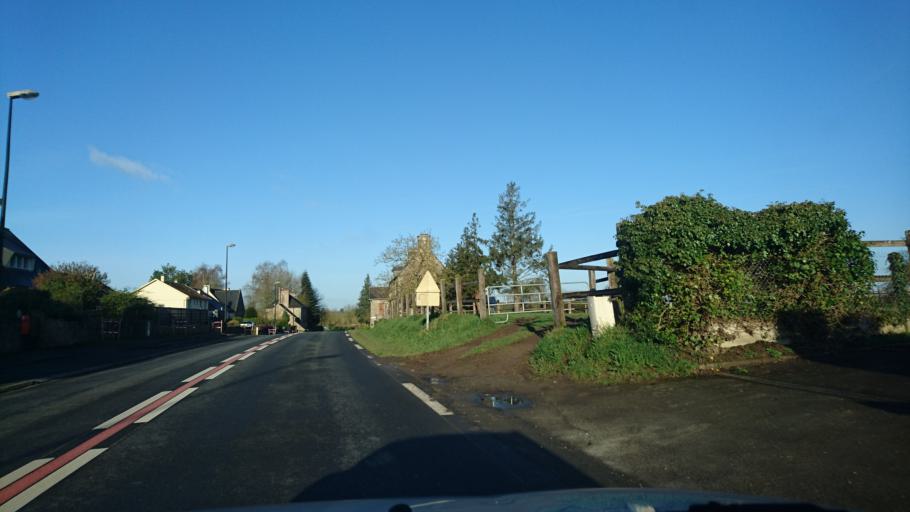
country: FR
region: Brittany
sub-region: Departement d'Ille-et-Vilaine
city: Pleine-Fougeres
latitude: 48.4959
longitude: -1.5913
